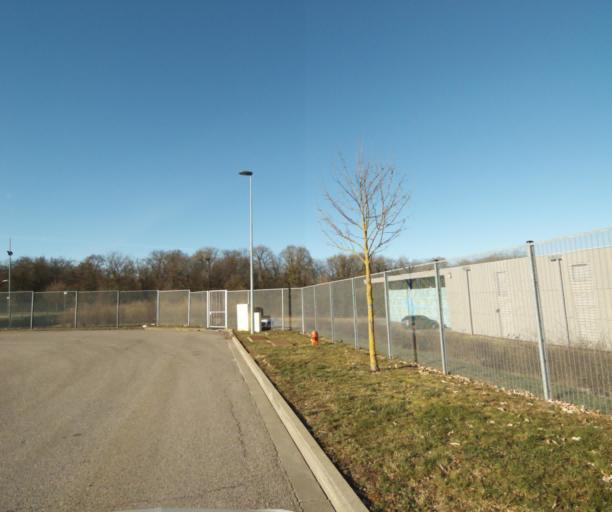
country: FR
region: Lorraine
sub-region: Departement de Meurthe-et-Moselle
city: Laxou
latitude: 48.7008
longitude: 6.1212
